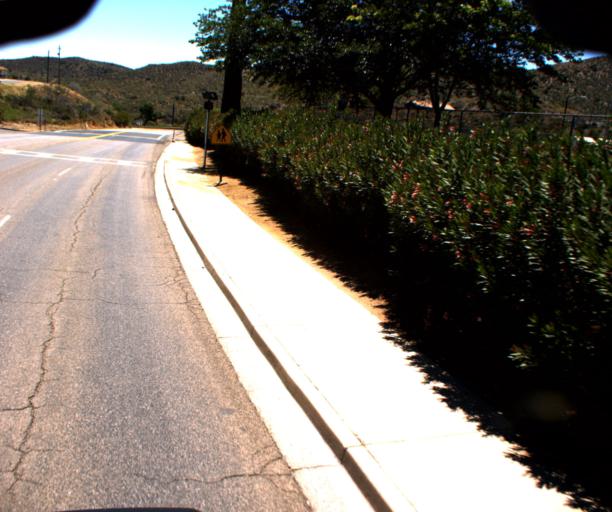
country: US
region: Arizona
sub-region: Yavapai County
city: Bagdad
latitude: 34.5692
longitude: -113.1757
